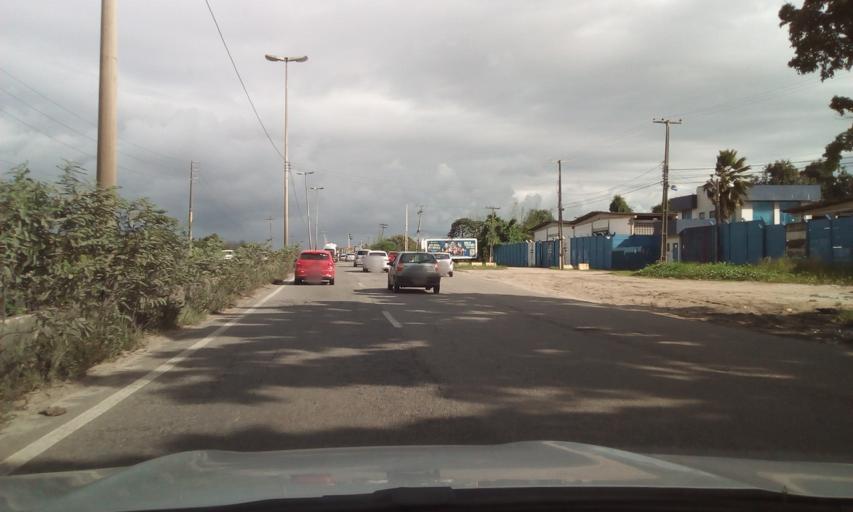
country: BR
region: Pernambuco
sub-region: Recife
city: Recife
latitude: -8.0218
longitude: -34.9428
